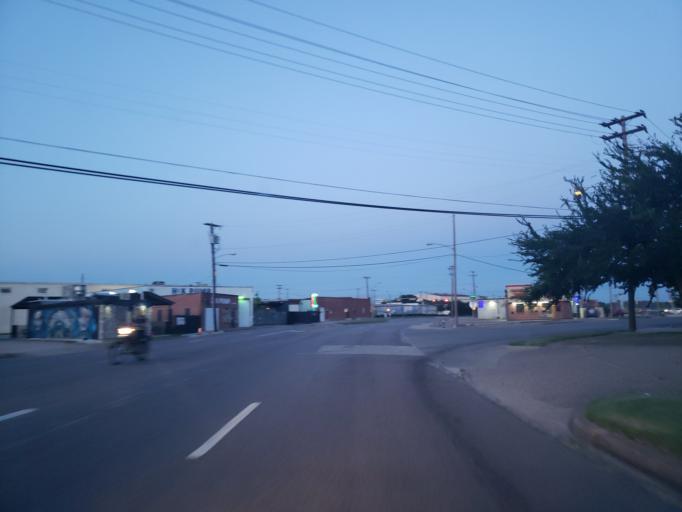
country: US
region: Texas
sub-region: Dallas County
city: Dallas
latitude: 32.7654
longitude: -96.7912
